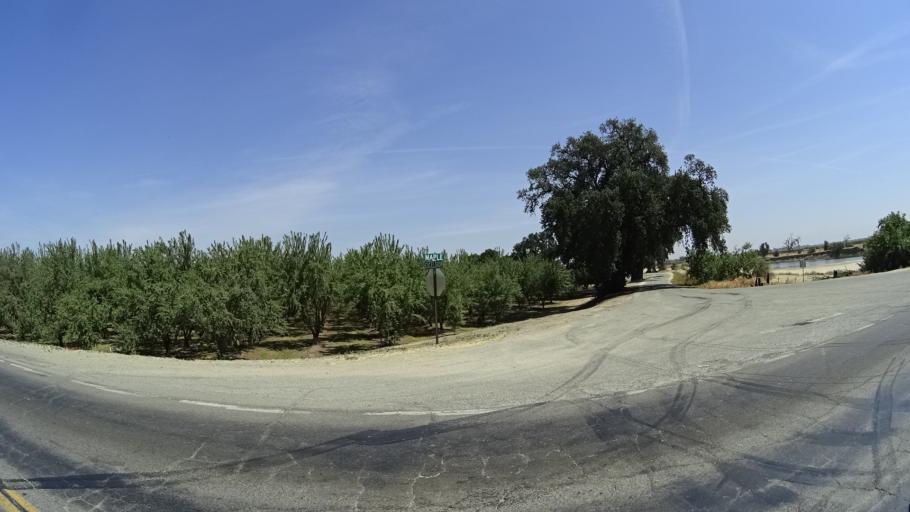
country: US
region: California
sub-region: Fresno County
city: Laton
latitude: 36.4019
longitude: -119.7534
